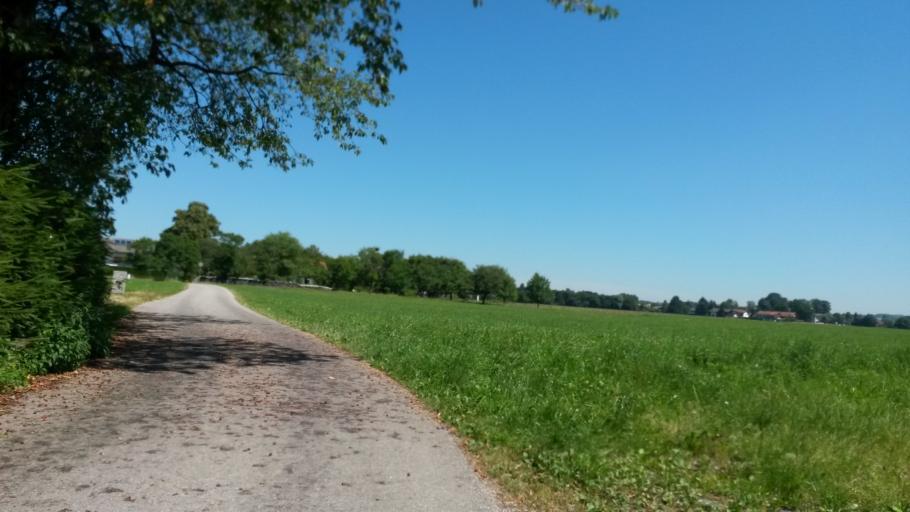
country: DE
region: Bavaria
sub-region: Upper Bavaria
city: Marquartstein
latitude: 47.7684
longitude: 12.4619
